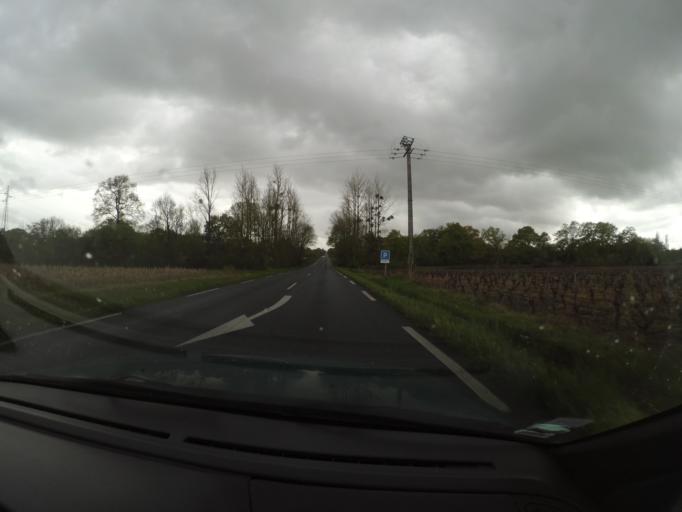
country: FR
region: Pays de la Loire
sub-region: Departement de la Loire-Atlantique
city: Vallet
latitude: 47.1927
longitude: -1.2511
